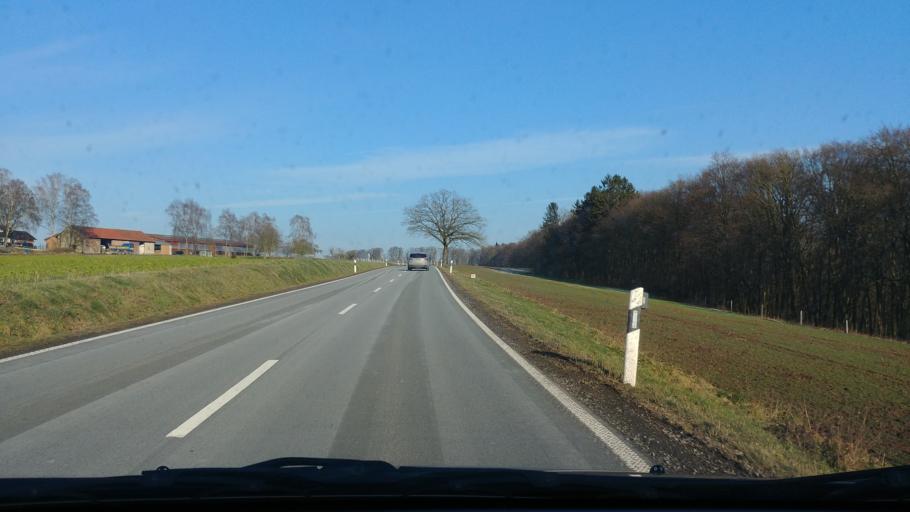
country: DE
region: Lower Saxony
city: Bad Karlshafen
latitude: 51.6167
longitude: 9.4374
